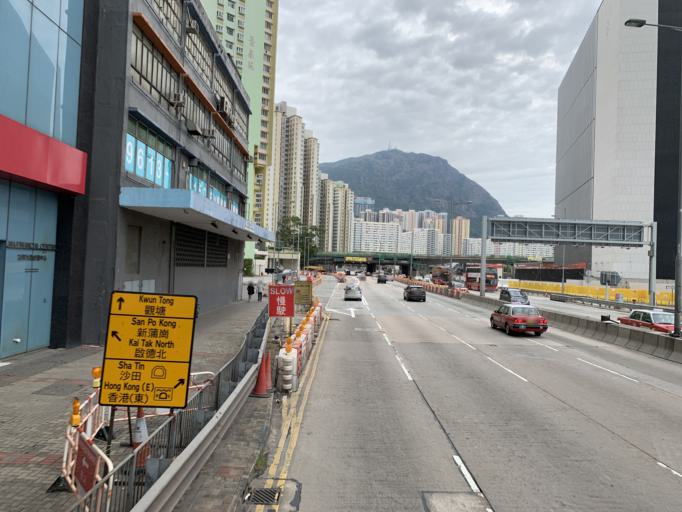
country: HK
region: Wong Tai Sin
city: Wong Tai Sin
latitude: 22.3344
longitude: 114.1997
